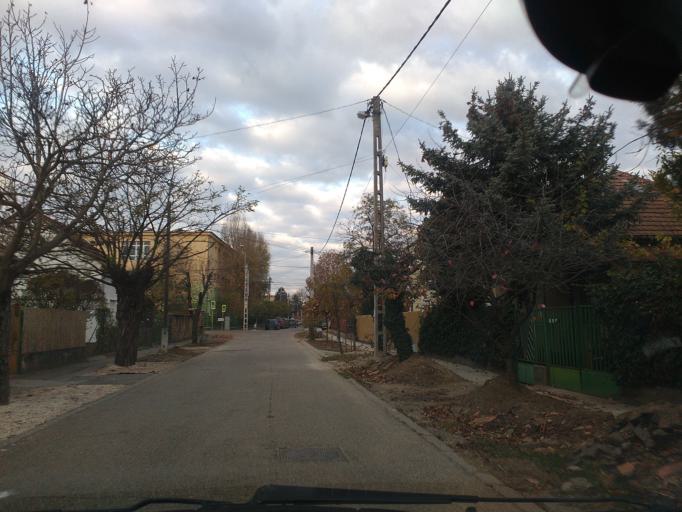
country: HU
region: Budapest
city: Budapest XVIII. keruelet
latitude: 47.4307
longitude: 19.2201
